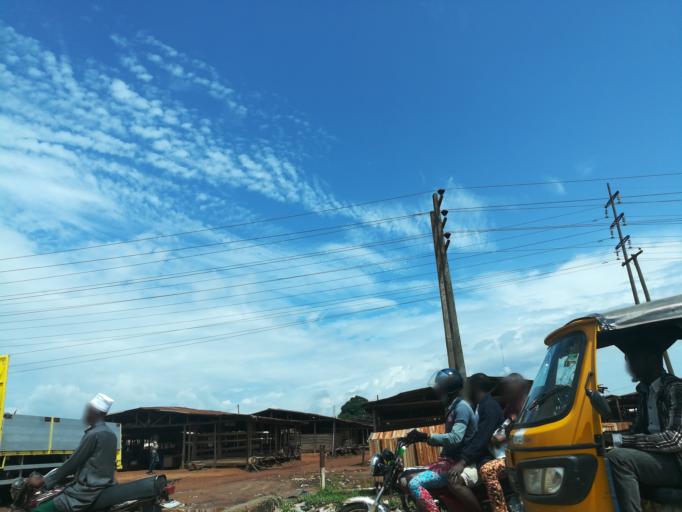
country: NG
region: Lagos
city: Ikorodu
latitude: 6.6396
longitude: 3.5144
